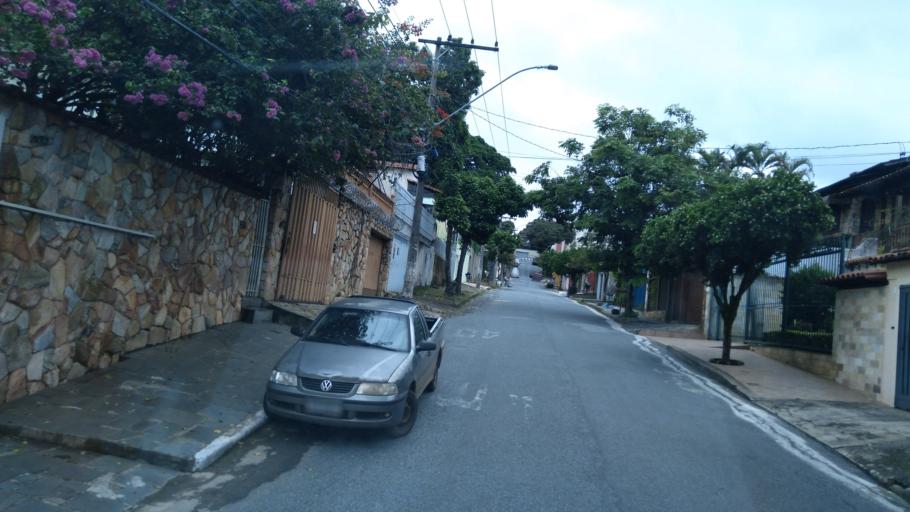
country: BR
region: Minas Gerais
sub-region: Belo Horizonte
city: Belo Horizonte
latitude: -19.9237
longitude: -43.9064
